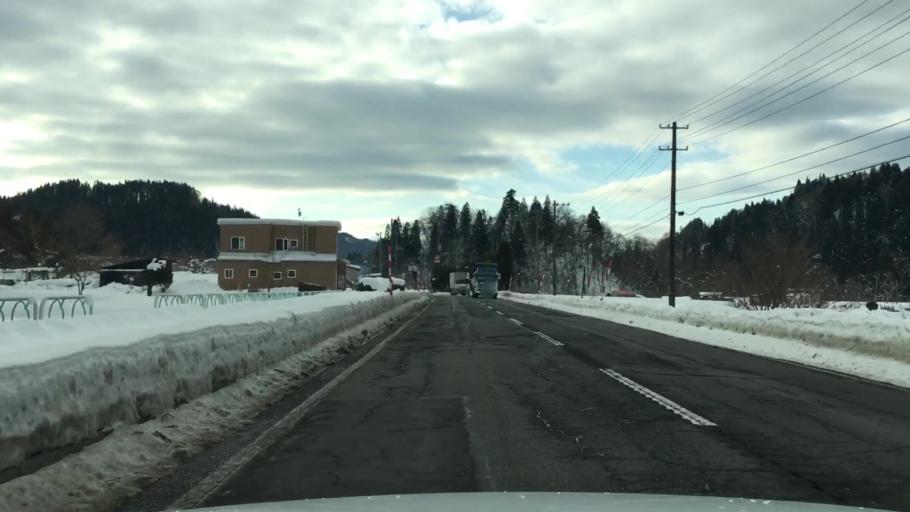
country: JP
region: Akita
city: Odate
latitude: 40.4529
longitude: 140.6354
